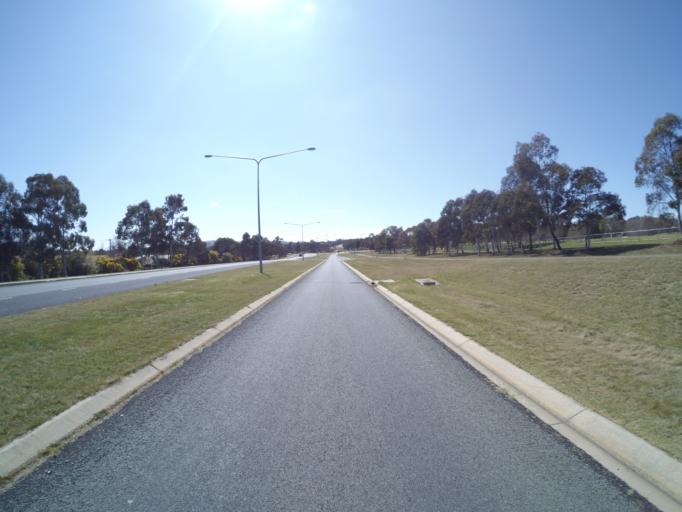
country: AU
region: Australian Capital Territory
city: Macarthur
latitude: -35.4394
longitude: 149.0892
